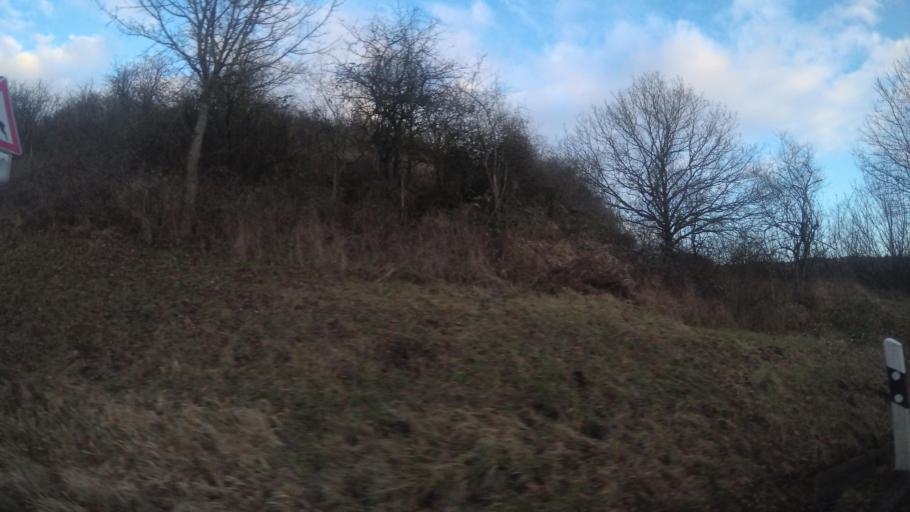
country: DE
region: Rheinland-Pfalz
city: Hochstatten
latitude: 49.7706
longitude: 7.8315
